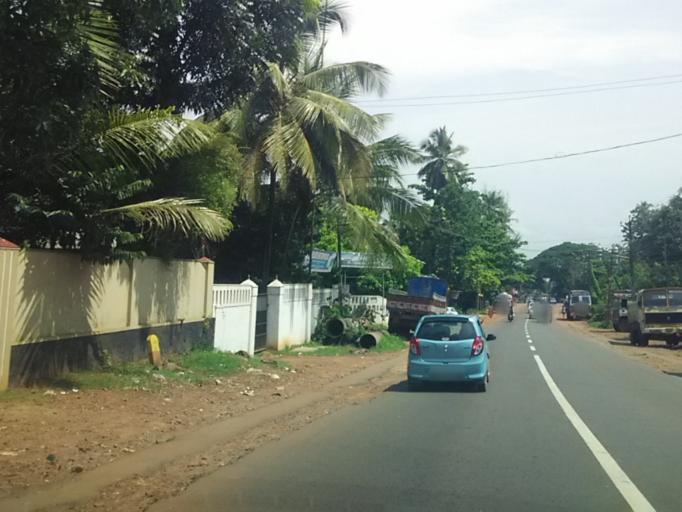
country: IN
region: Kerala
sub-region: Kozhikode
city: Kunnamangalam
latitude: 11.3254
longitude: 75.8850
